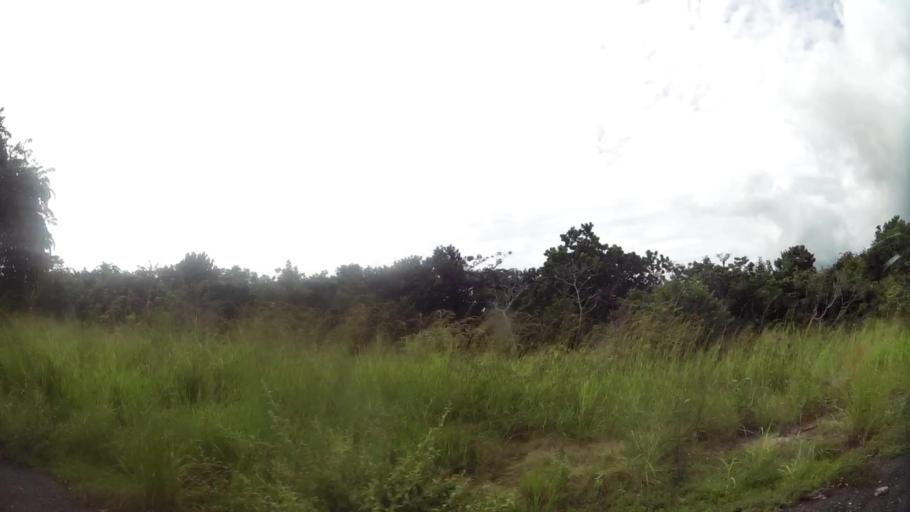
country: PA
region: Panama
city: Nueva Gorgona
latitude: 8.5383
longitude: -79.8977
